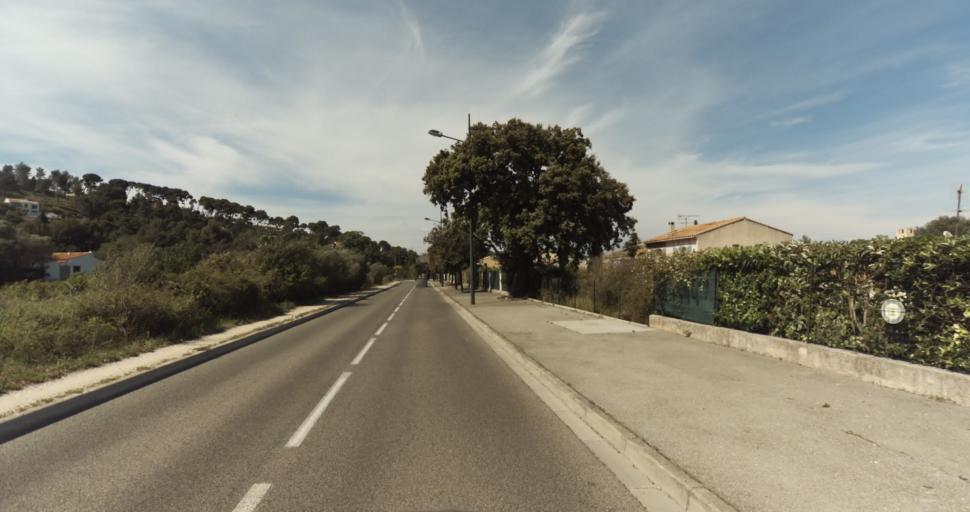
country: FR
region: Provence-Alpes-Cote d'Azur
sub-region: Departement du Var
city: Hyeres
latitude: 43.1001
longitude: 6.1213
